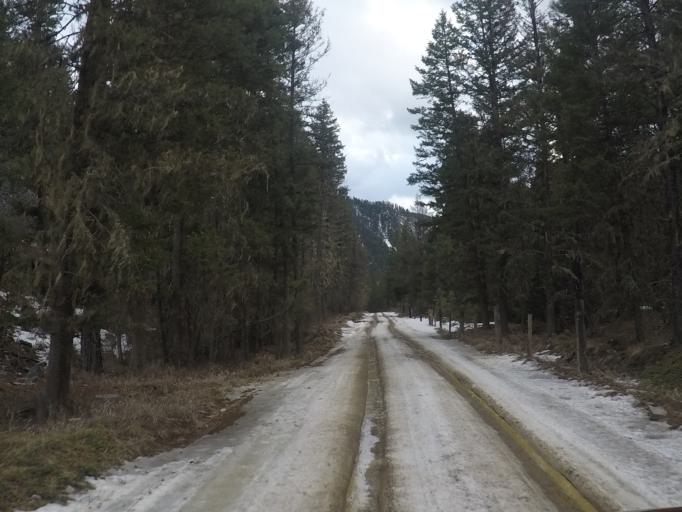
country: US
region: Montana
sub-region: Missoula County
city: Clinton
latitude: 46.5777
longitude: -113.6821
